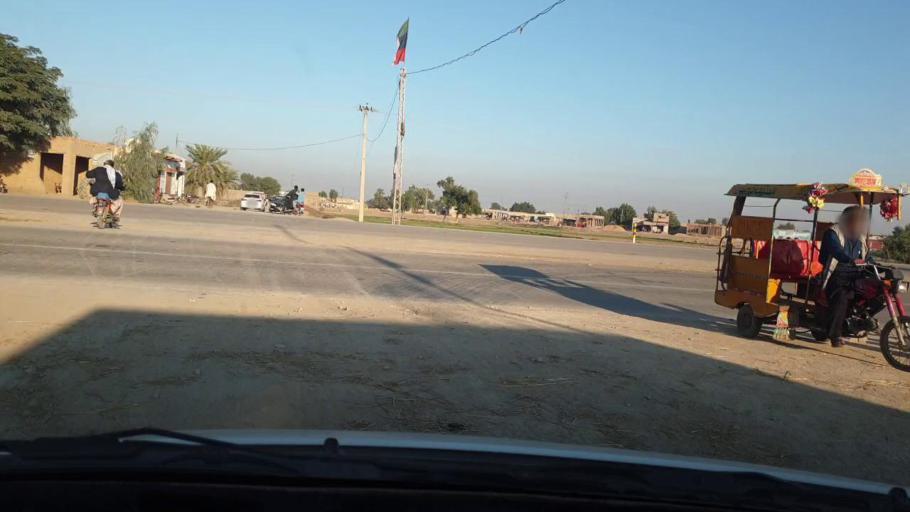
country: PK
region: Sindh
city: Khairpur Nathan Shah
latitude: 27.0751
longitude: 67.7265
